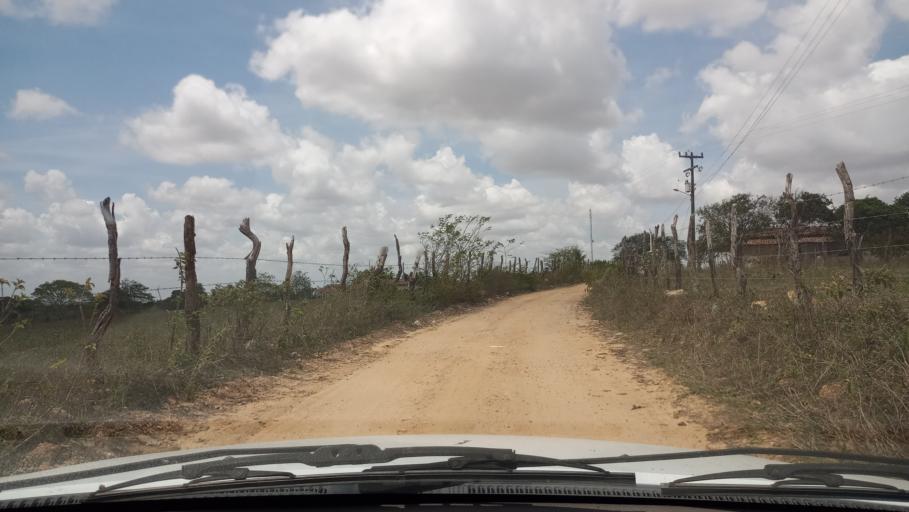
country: BR
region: Rio Grande do Norte
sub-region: Brejinho
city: Brejinho
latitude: -6.2704
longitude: -35.3452
